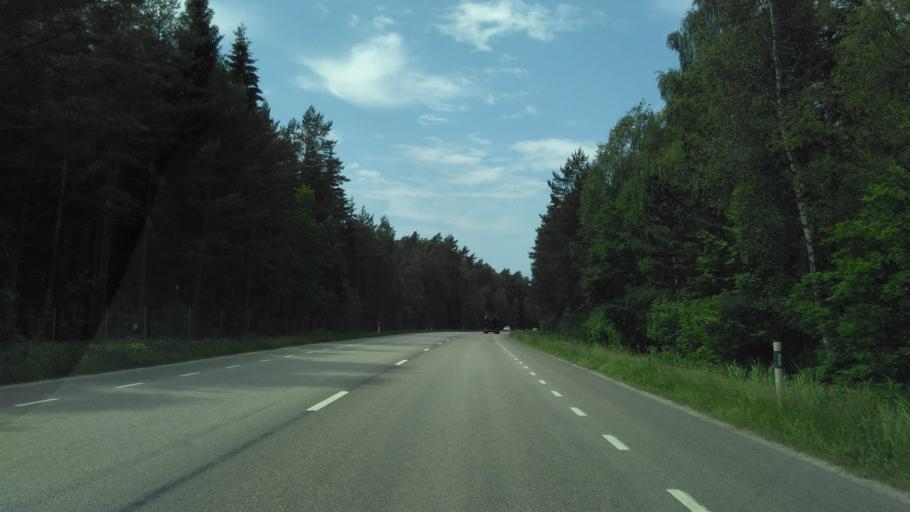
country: SE
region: Vaestra Goetaland
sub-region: Lidkopings Kommun
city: Lidkoping
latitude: 58.4869
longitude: 13.1640
